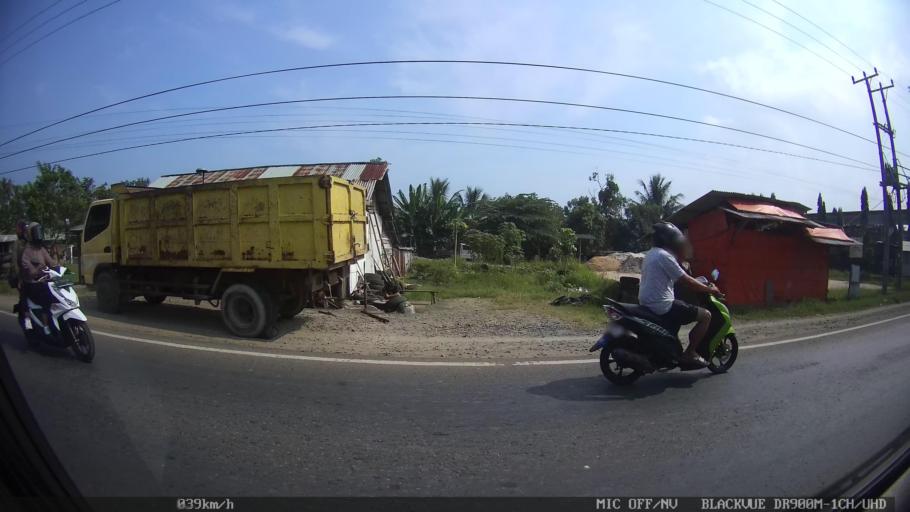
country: ID
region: Lampung
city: Gedongtataan
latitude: -5.3657
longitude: 105.1470
